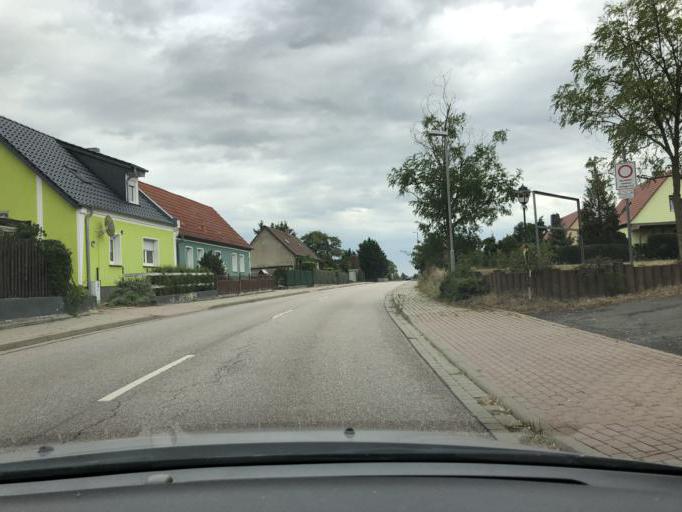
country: DE
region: Saxony-Anhalt
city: Wulfen
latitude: 51.7726
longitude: 11.9108
